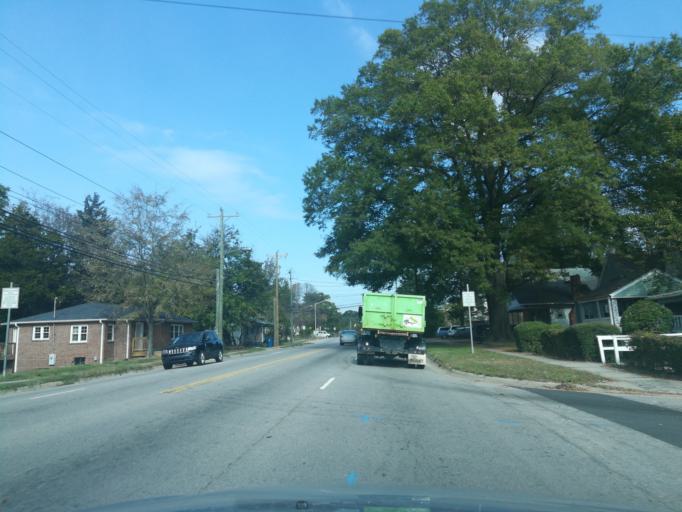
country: US
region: North Carolina
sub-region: Durham County
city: Durham
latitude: 35.9771
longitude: -78.8927
